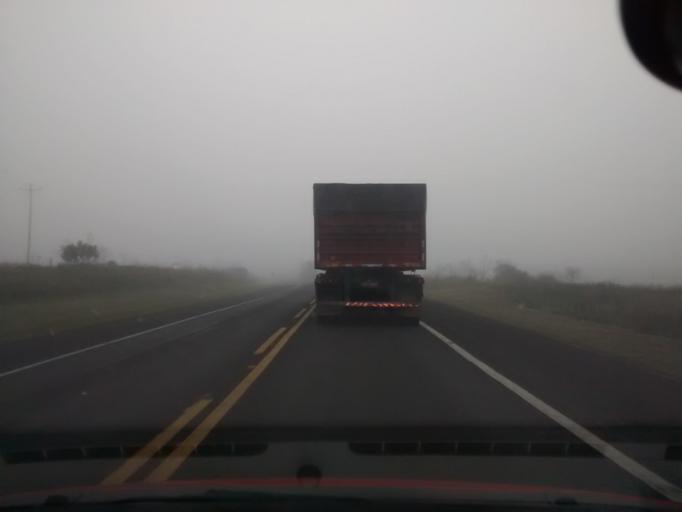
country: BR
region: Rio Grande do Sul
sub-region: Vacaria
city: Vacaria
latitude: -28.3674
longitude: -50.8338
